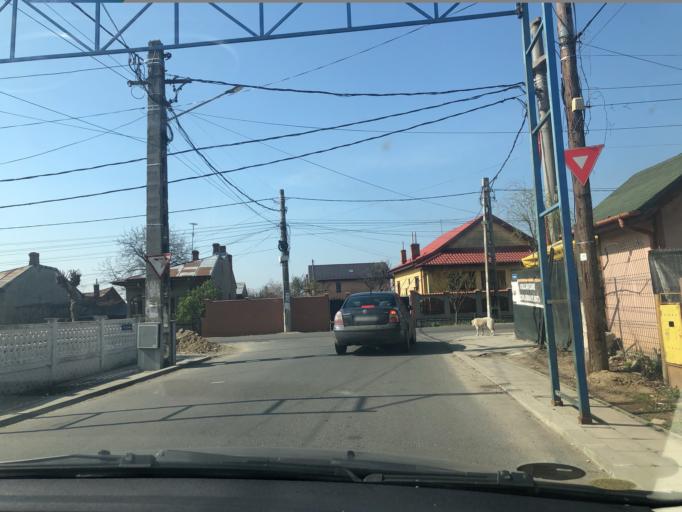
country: RO
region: Ilfov
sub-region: Comuna Clinceni
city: Clinceni
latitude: 44.3725
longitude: 25.9577
